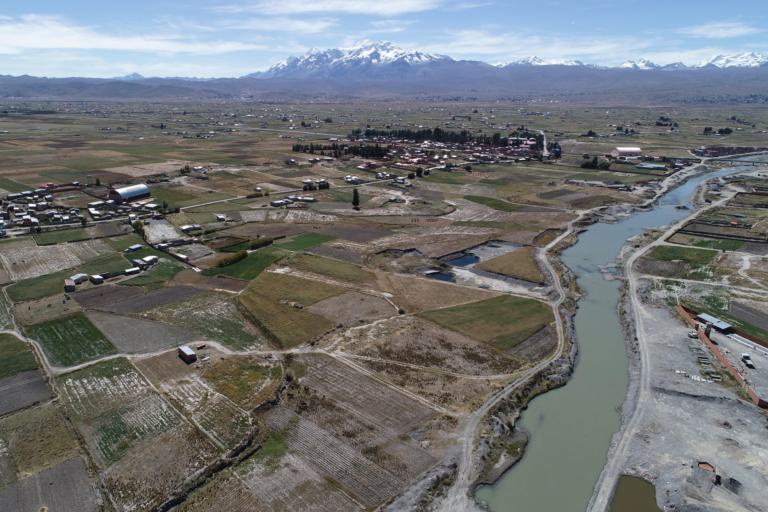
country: BO
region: La Paz
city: Achacachi
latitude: -16.0411
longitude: -68.6962
